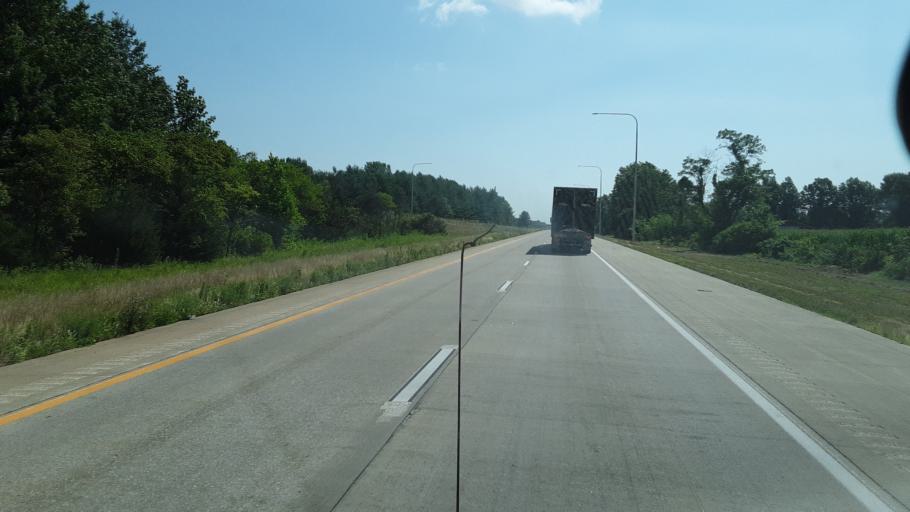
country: US
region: Illinois
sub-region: Effingham County
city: Teutopolis
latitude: 39.1490
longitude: -88.5077
